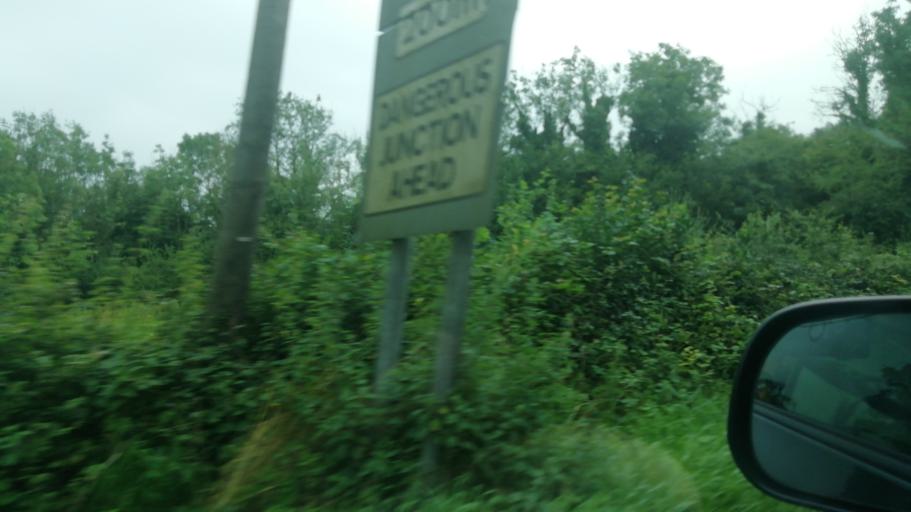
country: IE
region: Munster
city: Fethard
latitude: 52.5276
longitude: -7.6813
